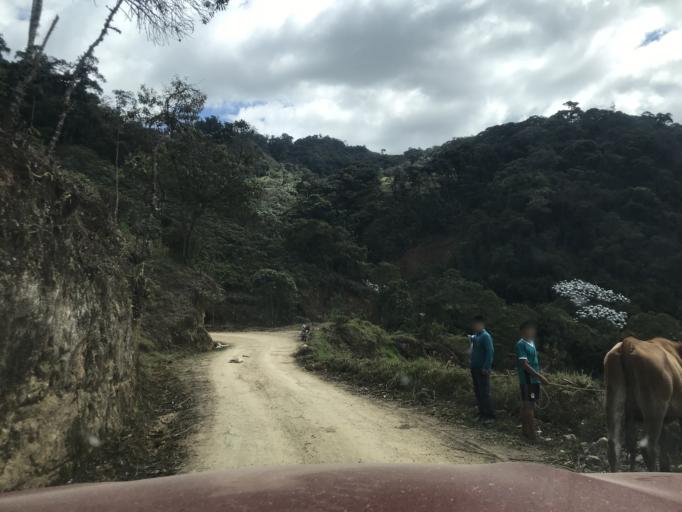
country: PE
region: Cajamarca
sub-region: Provincia de Chota
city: Querocoto
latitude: -6.3495
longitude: -79.0582
